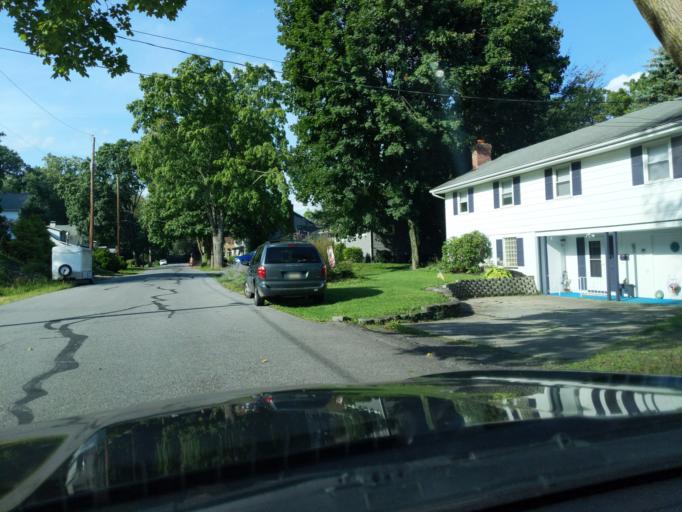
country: US
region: Pennsylvania
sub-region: Blair County
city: Lakemont
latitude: 40.4814
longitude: -78.4087
